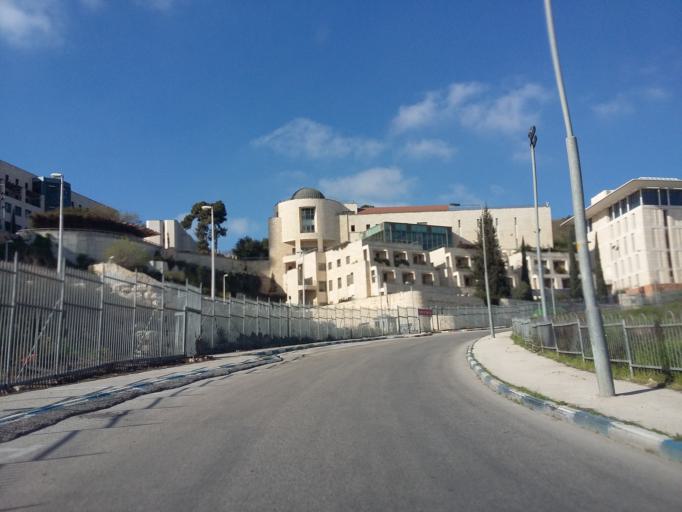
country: PS
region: West Bank
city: East Jerusalem
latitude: 31.7941
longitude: 35.2468
